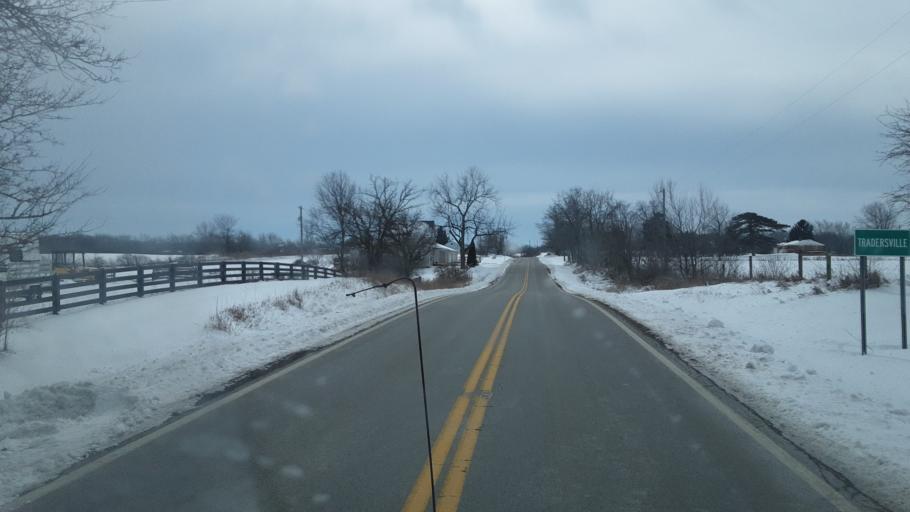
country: US
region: Ohio
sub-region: Madison County
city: Choctaw Lake
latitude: 40.0023
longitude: -83.4986
